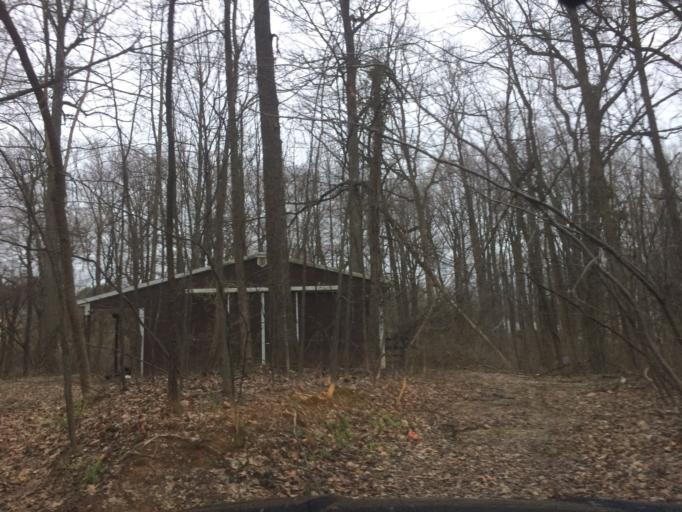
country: US
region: Maryland
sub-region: Howard County
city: Highland
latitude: 39.2336
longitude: -76.9863
